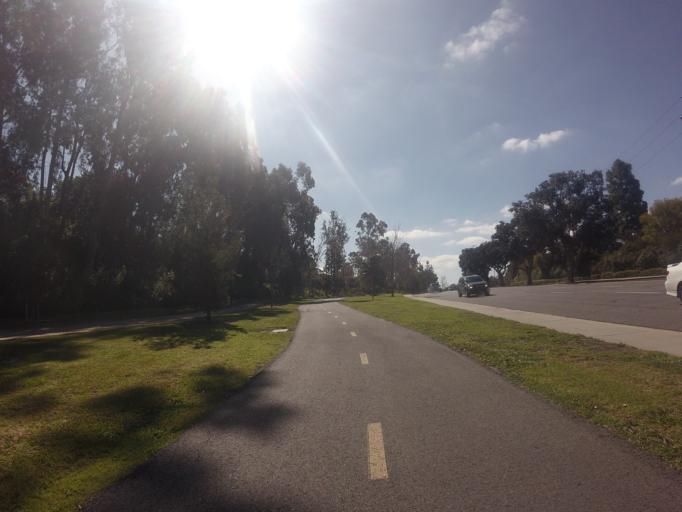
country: US
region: California
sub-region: Orange County
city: Laguna Hills
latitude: 33.5985
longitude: -117.7014
